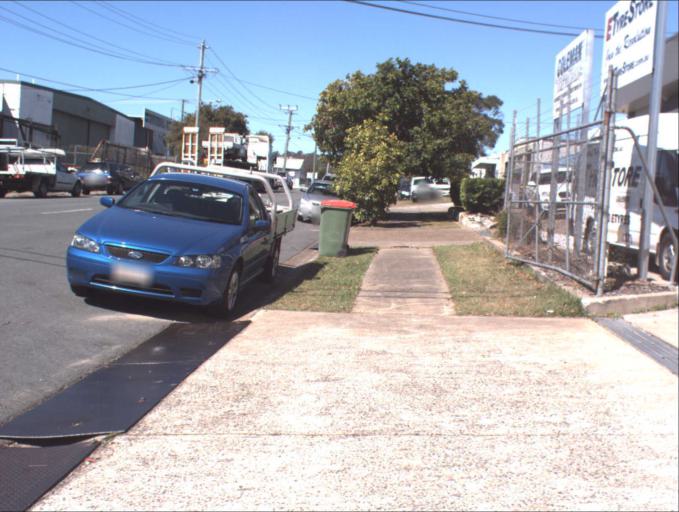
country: AU
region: Queensland
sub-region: Logan
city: Springwood
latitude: -27.6294
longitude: 153.1268
